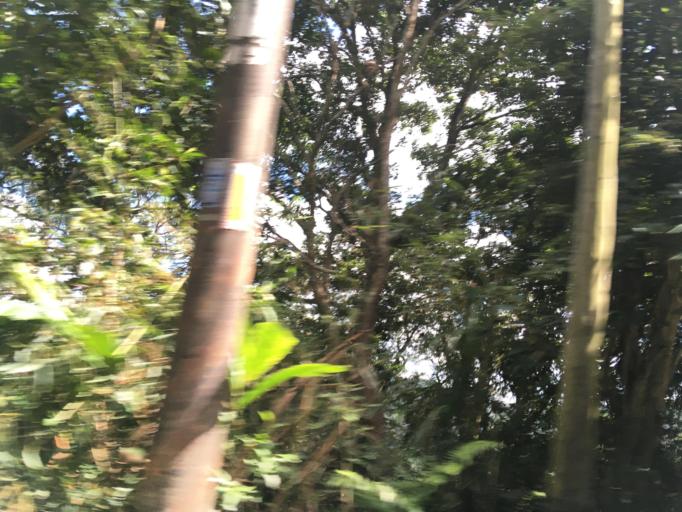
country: TW
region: Taipei
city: Taipei
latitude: 24.9352
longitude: 121.5818
